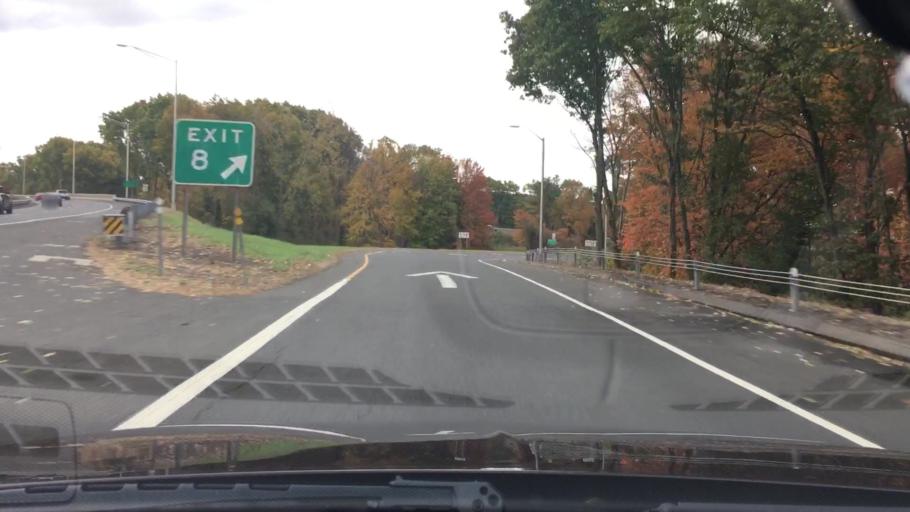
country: US
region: Connecticut
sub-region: Hartford County
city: Glastonbury
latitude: 41.7159
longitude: -72.5998
